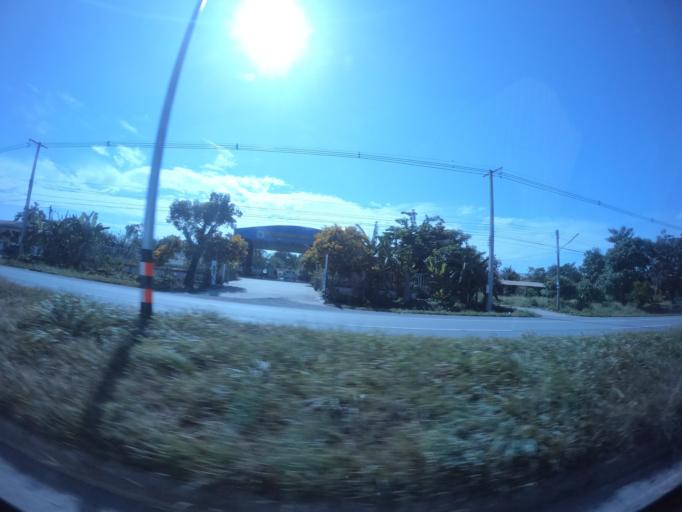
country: TH
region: Nakhon Nayok
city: Ban Na
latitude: 14.2460
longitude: 101.0717
